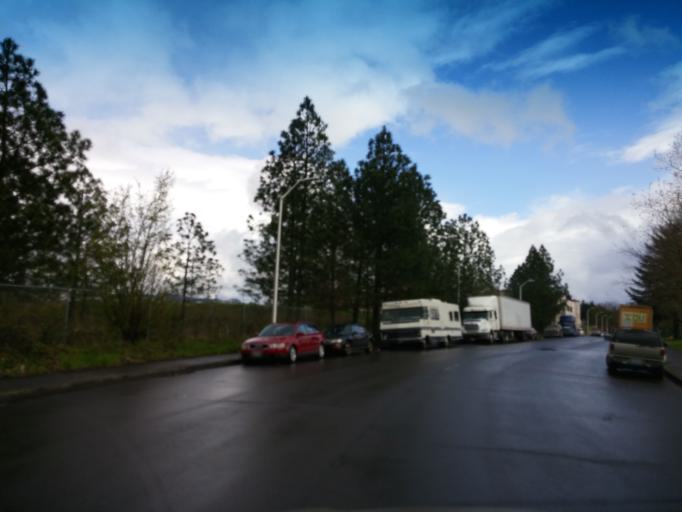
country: US
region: Oregon
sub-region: Washington County
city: Aloha
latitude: 45.5085
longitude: -122.8514
